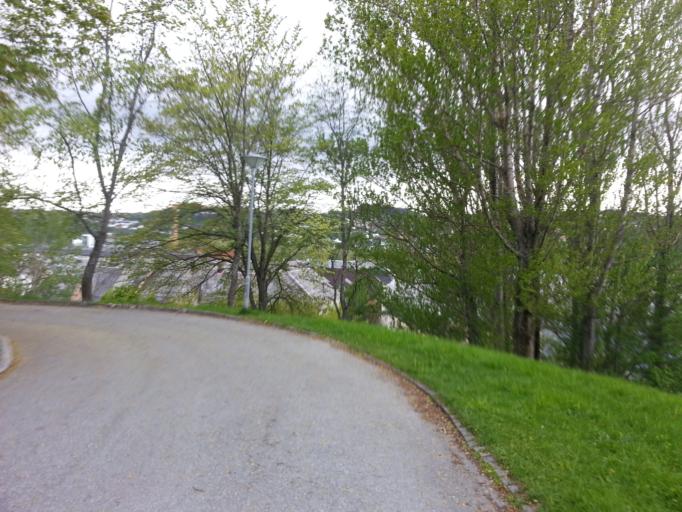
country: NO
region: Sor-Trondelag
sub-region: Trondheim
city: Trondheim
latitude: 63.4187
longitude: 10.3988
